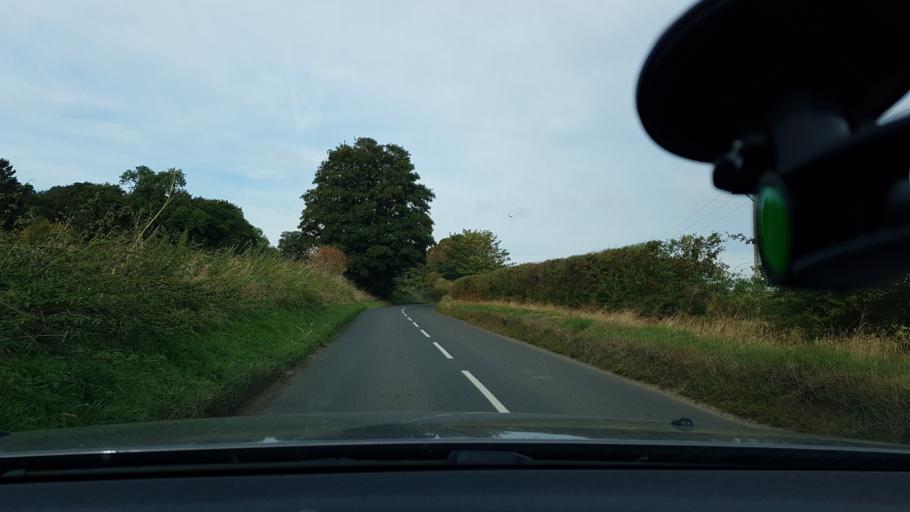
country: GB
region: England
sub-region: West Berkshire
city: Kintbury
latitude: 51.4052
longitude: -1.4751
